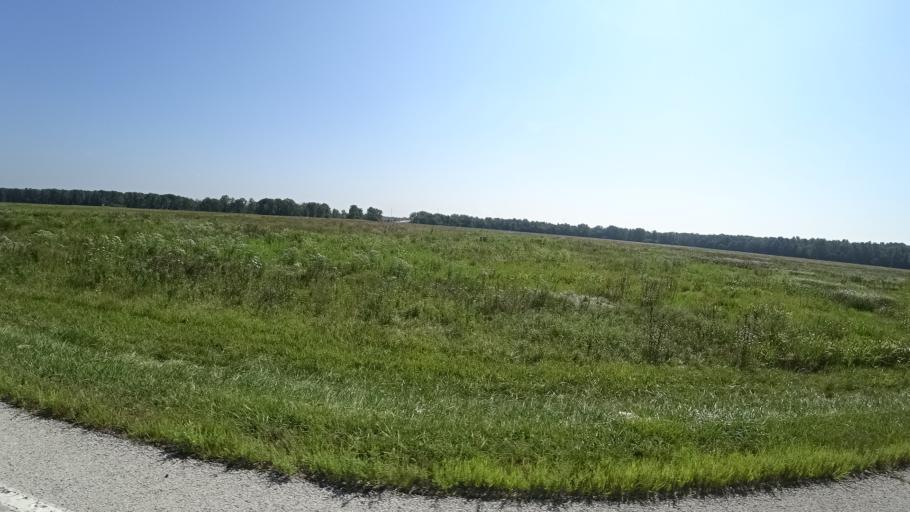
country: US
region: Illinois
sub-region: Cook County
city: Country Club Hills
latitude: 41.5416
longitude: -87.7518
